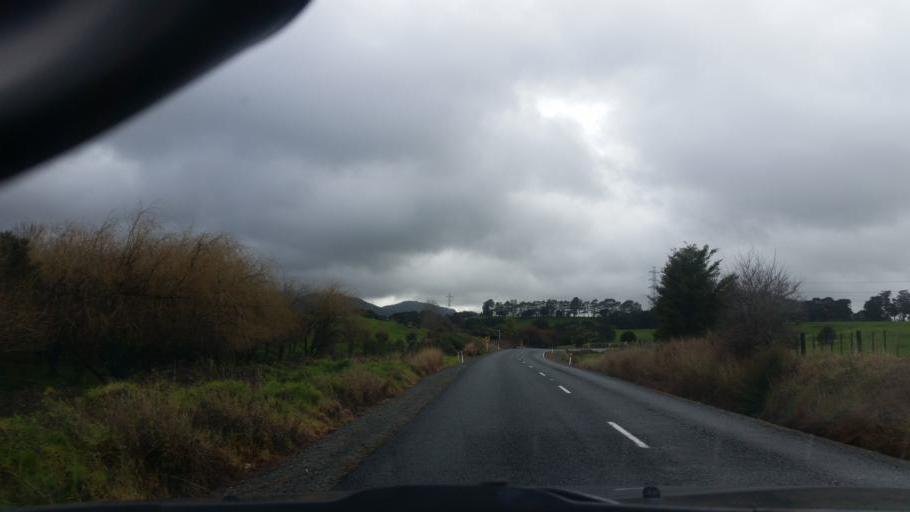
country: NZ
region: Auckland
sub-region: Auckland
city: Wellsford
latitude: -36.1674
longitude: 174.4228
